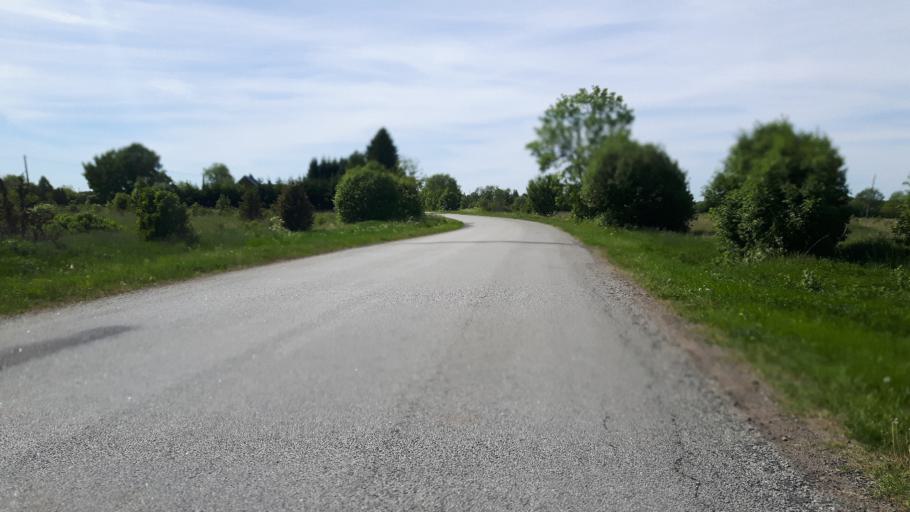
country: EE
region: Harju
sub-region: Anija vald
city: Kehra
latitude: 59.4688
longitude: 25.3091
